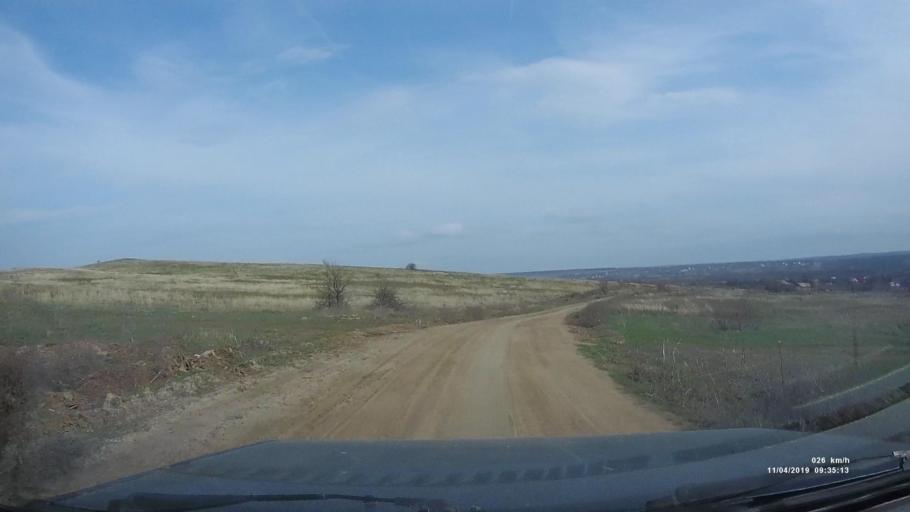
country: RU
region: Rostov
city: Staraya Stanitsa
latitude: 48.2715
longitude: 40.3716
